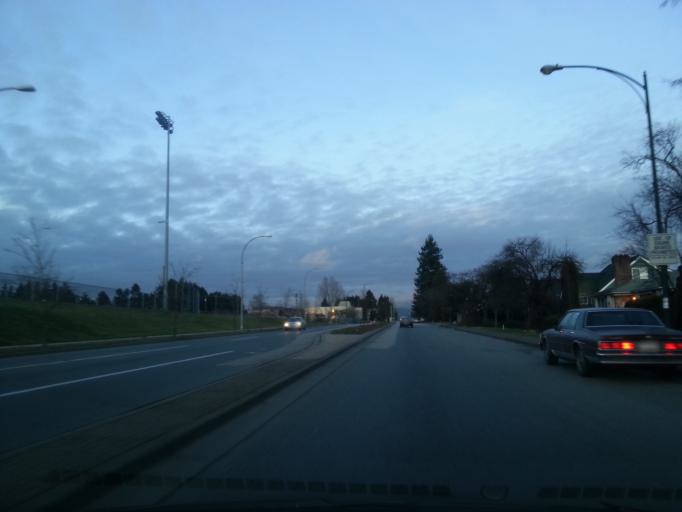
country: CA
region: British Columbia
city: New Westminster
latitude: 49.2064
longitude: -122.9509
